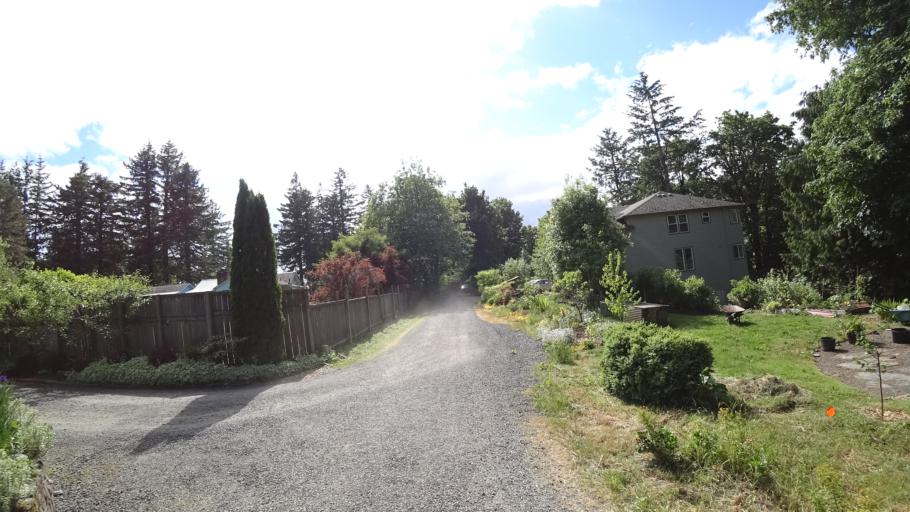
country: US
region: Oregon
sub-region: Washington County
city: Cedar Mill
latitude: 45.5778
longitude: -122.7935
